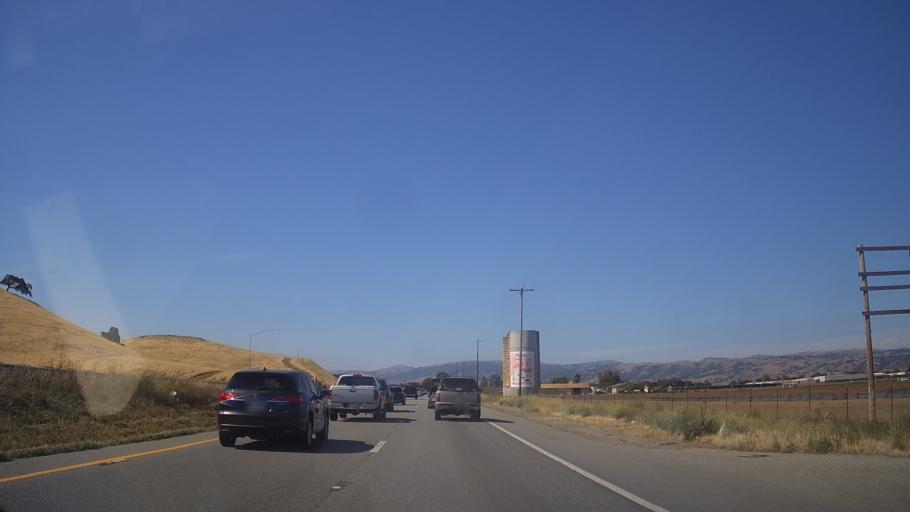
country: US
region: California
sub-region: Santa Clara County
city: Gilroy
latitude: 36.9549
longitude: -121.5507
